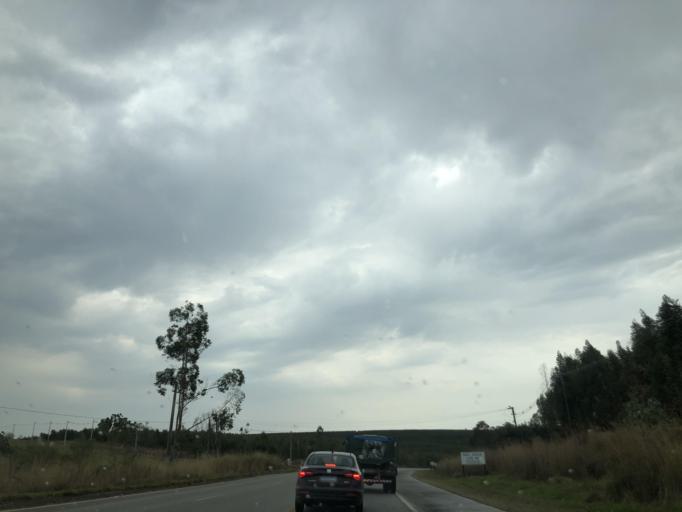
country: BR
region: Sao Paulo
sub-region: Salto De Pirapora
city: Salto de Pirapora
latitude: -23.6859
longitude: -47.6065
